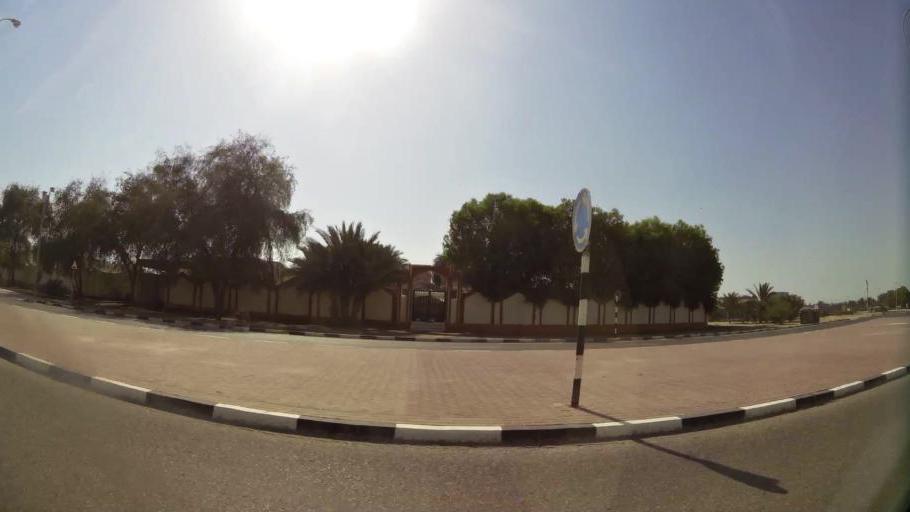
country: AE
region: Ajman
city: Ajman
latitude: 25.4115
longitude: 55.4672
